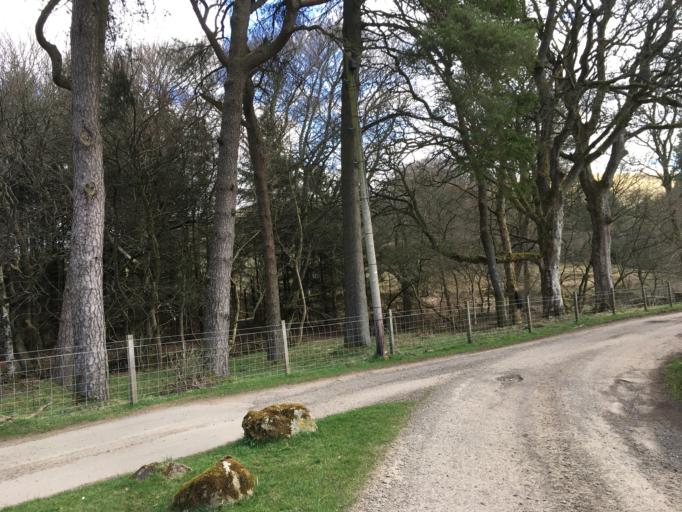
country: GB
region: Scotland
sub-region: The Scottish Borders
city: West Linton
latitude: 55.7795
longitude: -3.3943
